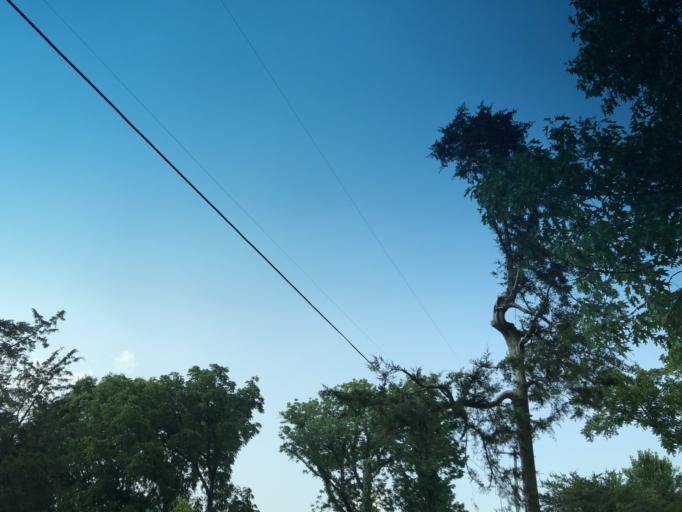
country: US
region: Tennessee
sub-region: Davidson County
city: Goodlettsville
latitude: 36.2755
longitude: -86.7212
